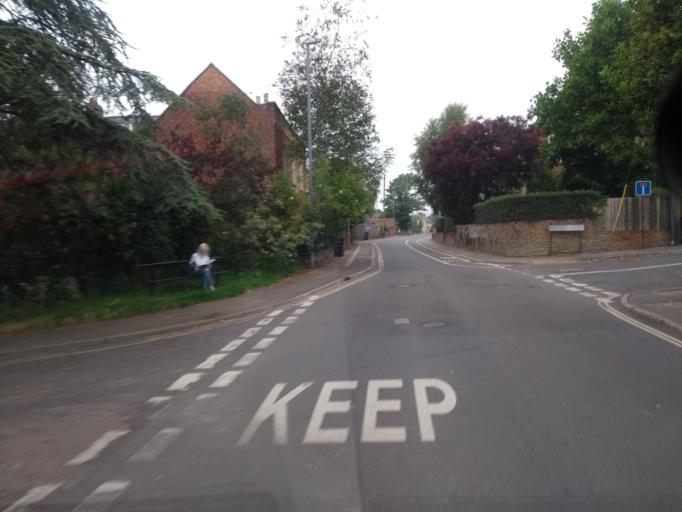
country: GB
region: England
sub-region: Dorset
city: Bridport
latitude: 50.7344
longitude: -2.7656
